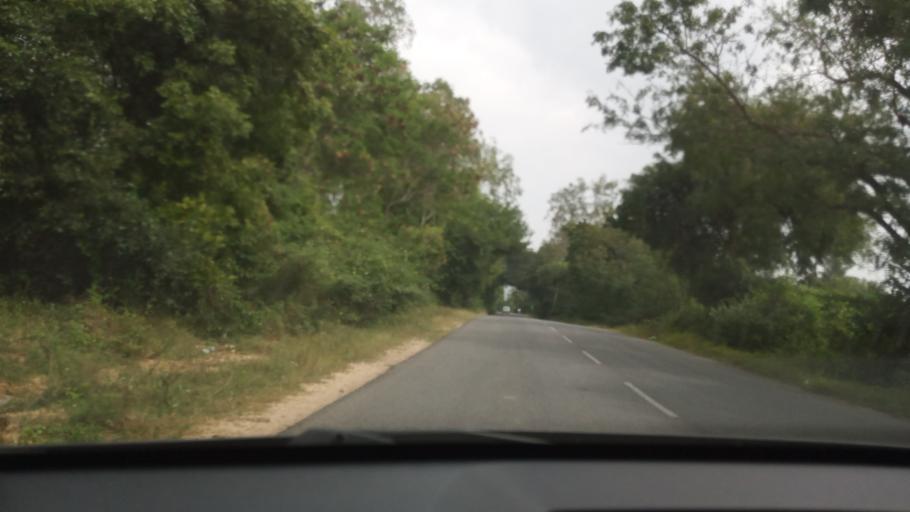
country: IN
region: Andhra Pradesh
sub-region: Chittoor
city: Pakala
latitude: 13.6562
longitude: 78.8499
